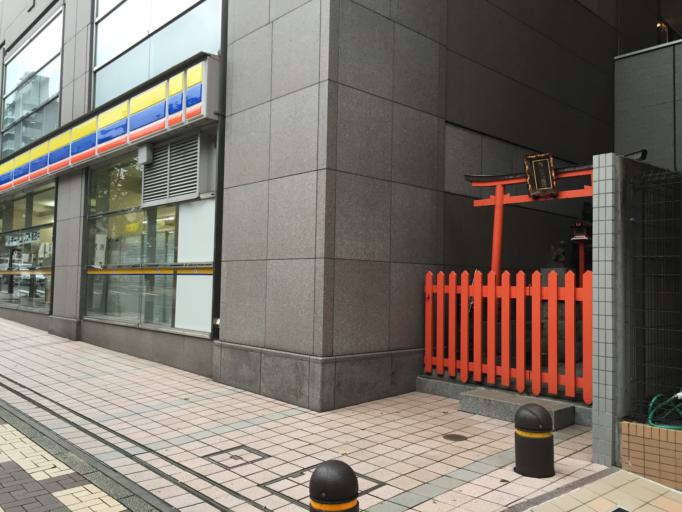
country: JP
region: Kanagawa
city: Yokohama
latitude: 35.4466
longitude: 139.6318
